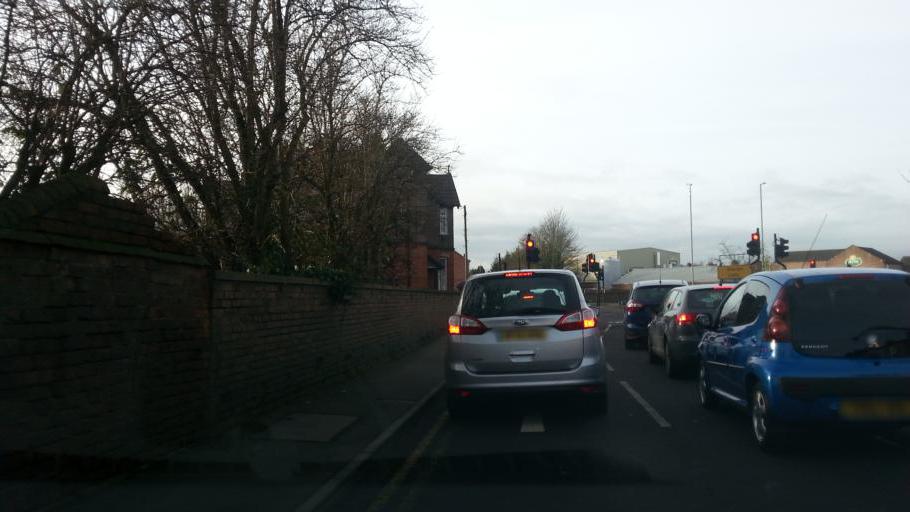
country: GB
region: England
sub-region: Leicestershire
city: Melton Mowbray
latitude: 52.7657
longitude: -0.8784
